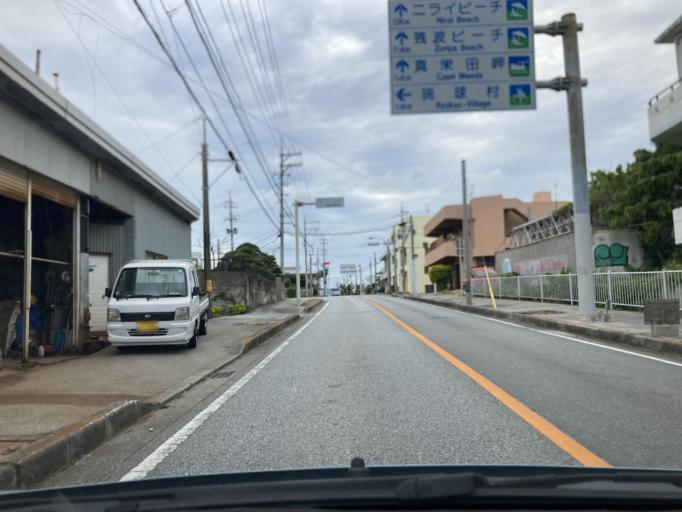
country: JP
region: Okinawa
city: Ishikawa
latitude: 26.4373
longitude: 127.7793
